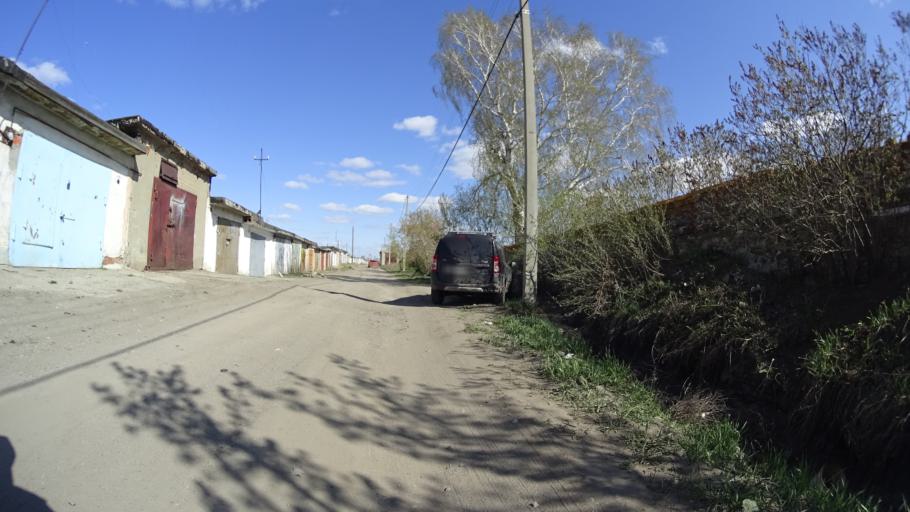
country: RU
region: Chelyabinsk
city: Troitsk
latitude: 54.0833
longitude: 61.5231
